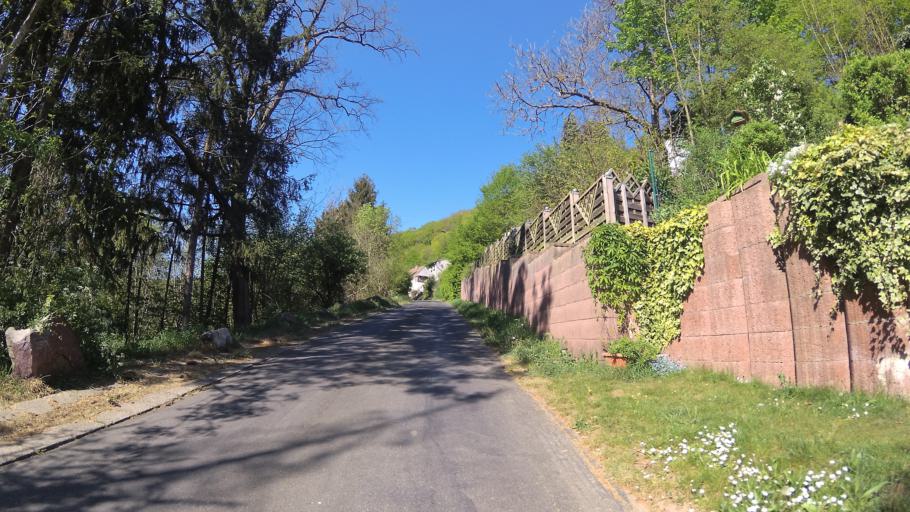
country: DE
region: Saarland
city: Hangard
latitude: 49.3833
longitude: 7.2150
